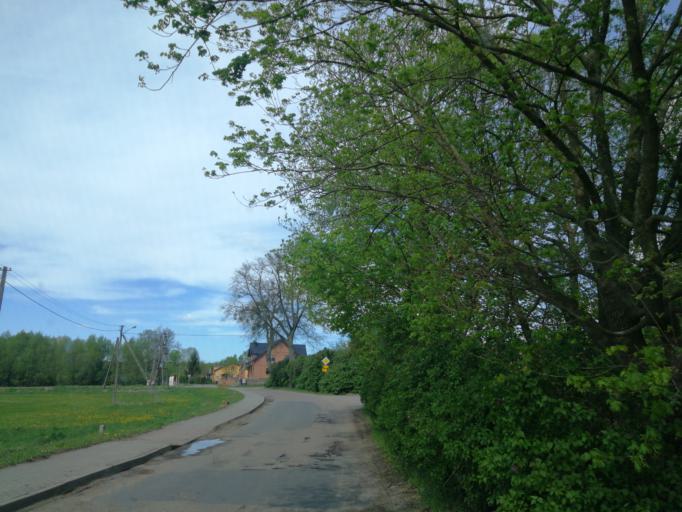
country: PL
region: Warmian-Masurian Voivodeship
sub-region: Powiat ilawski
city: Lubawa
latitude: 53.5824
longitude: 19.7332
